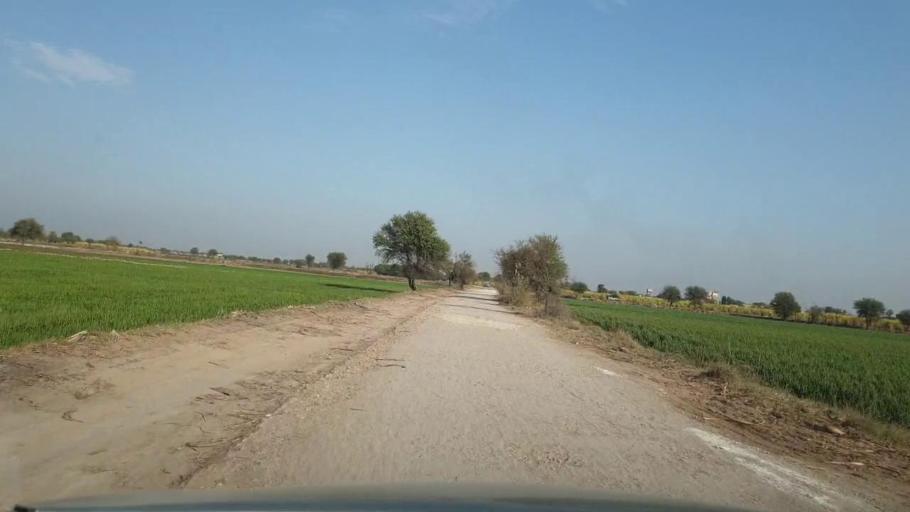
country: PK
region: Sindh
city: Tando Allahyar
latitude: 25.5936
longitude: 68.6691
